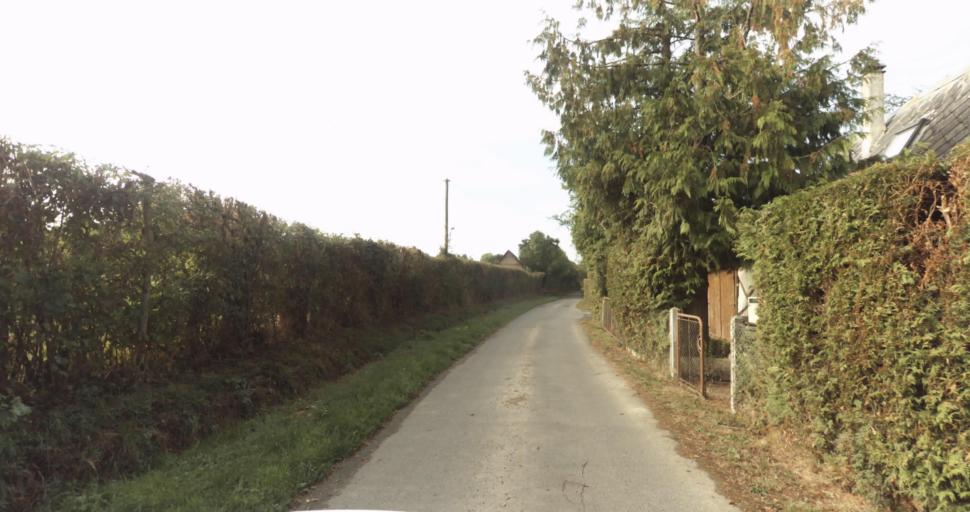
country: FR
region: Lower Normandy
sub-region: Departement de l'Orne
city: Gace
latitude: 48.9096
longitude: 0.3162
